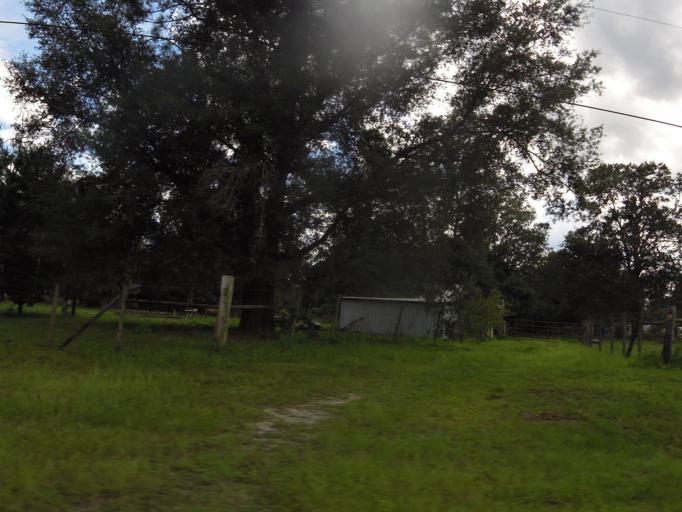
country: US
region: Florida
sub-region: Clay County
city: Green Cove Springs
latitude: 29.9884
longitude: -81.7202
